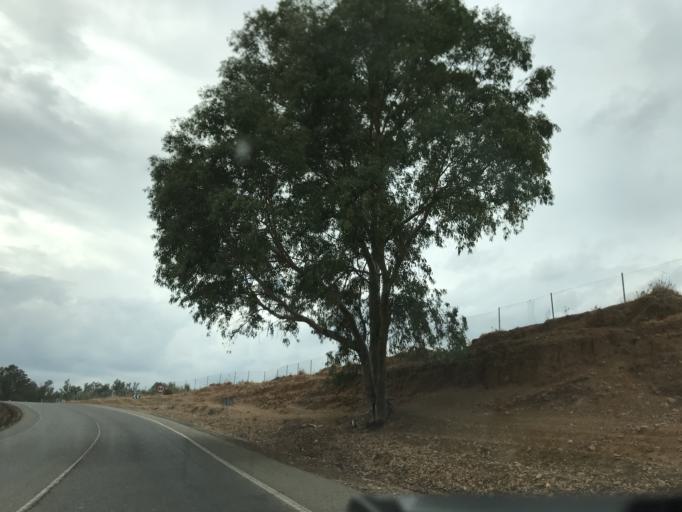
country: ES
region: Andalusia
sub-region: Provincia de Sevilla
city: Villanueva del Rio y Minas
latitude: 37.6432
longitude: -5.7400
